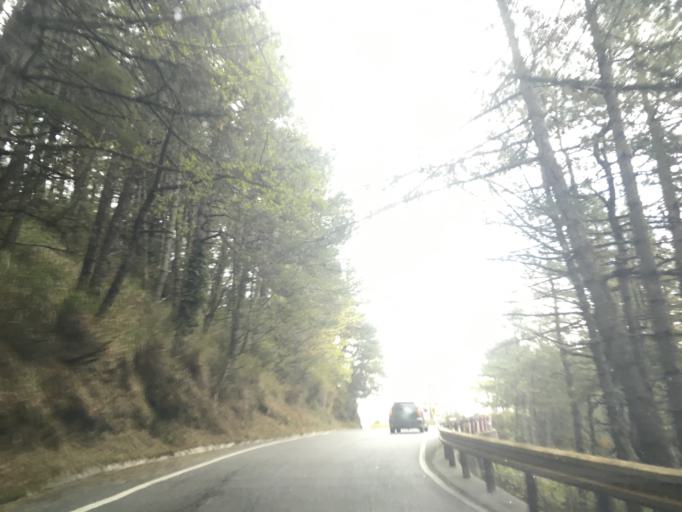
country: TW
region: Taiwan
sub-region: Hualien
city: Hualian
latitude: 24.1793
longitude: 121.3035
